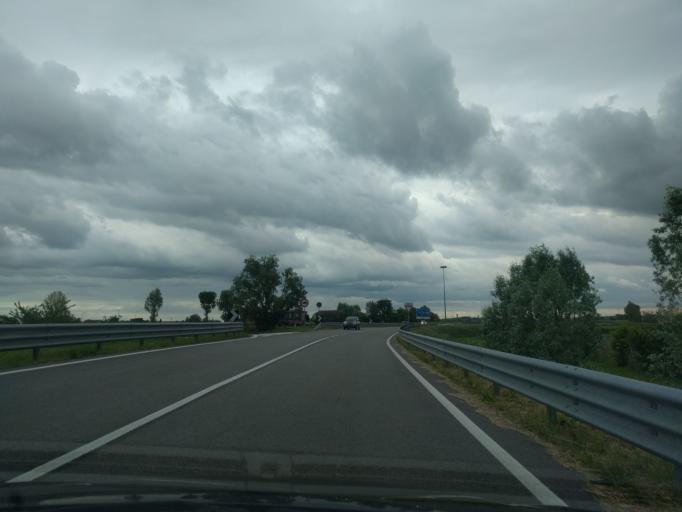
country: IT
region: Veneto
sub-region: Provincia di Rovigo
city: Buso
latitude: 45.0781
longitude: 11.8545
